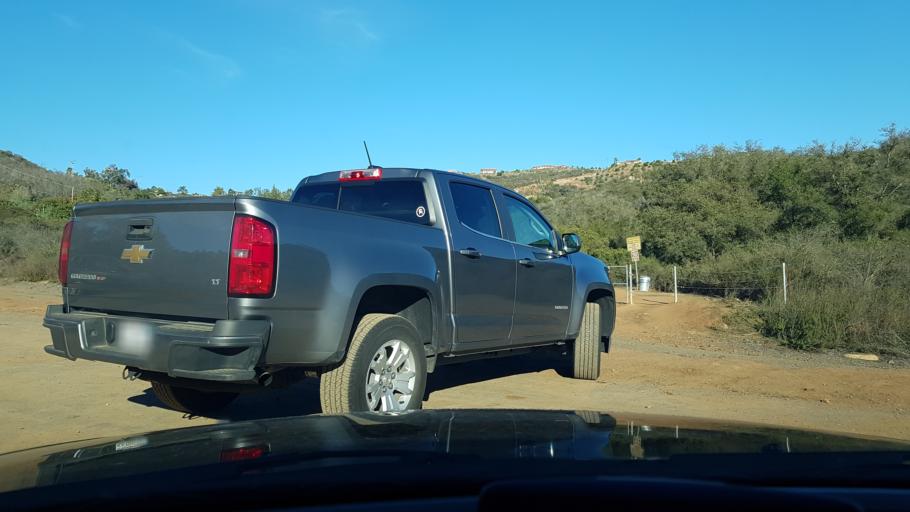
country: US
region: California
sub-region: San Diego County
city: Hidden Meadows
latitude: 33.2097
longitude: -117.0858
